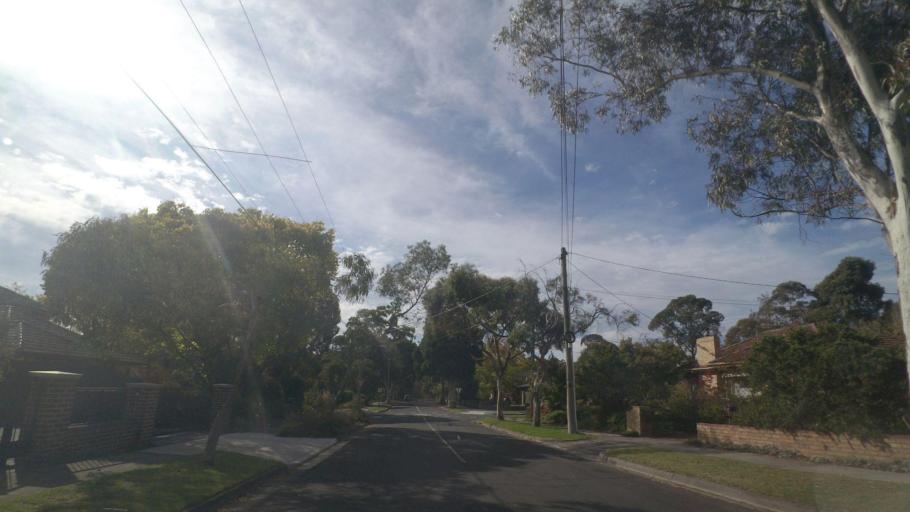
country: AU
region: Victoria
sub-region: Whitehorse
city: Blackburn
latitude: -37.8287
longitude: 145.1434
